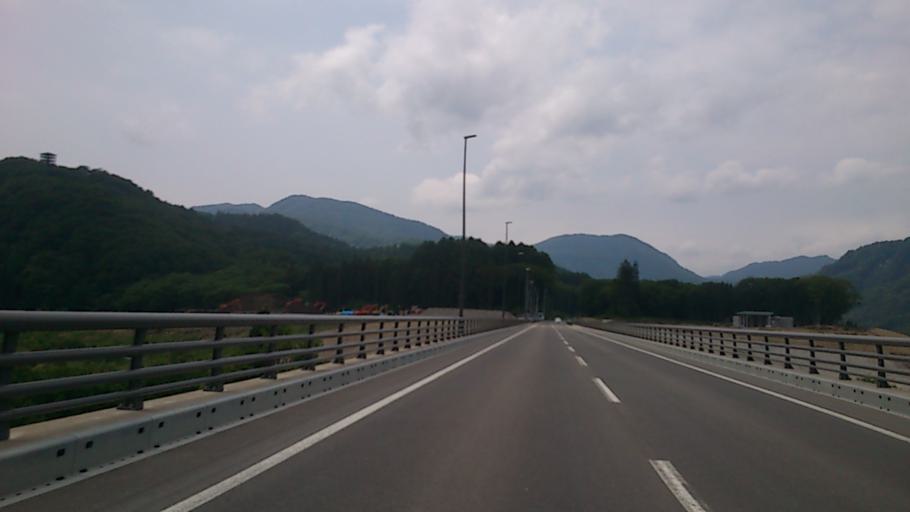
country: JP
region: Aomori
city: Hirosaki
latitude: 40.5212
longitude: 140.2228
